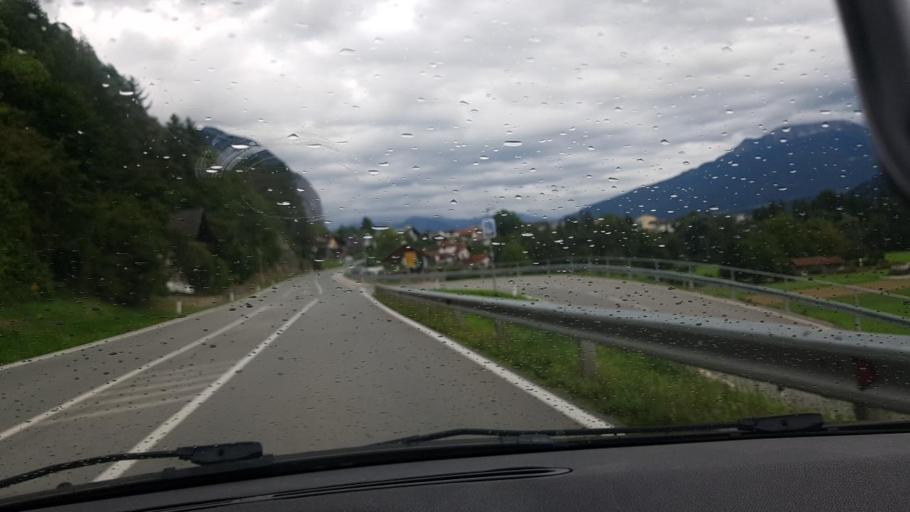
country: AT
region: Tyrol
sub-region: Politischer Bezirk Innsbruck Land
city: Zirl
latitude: 47.2777
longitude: 11.2295
